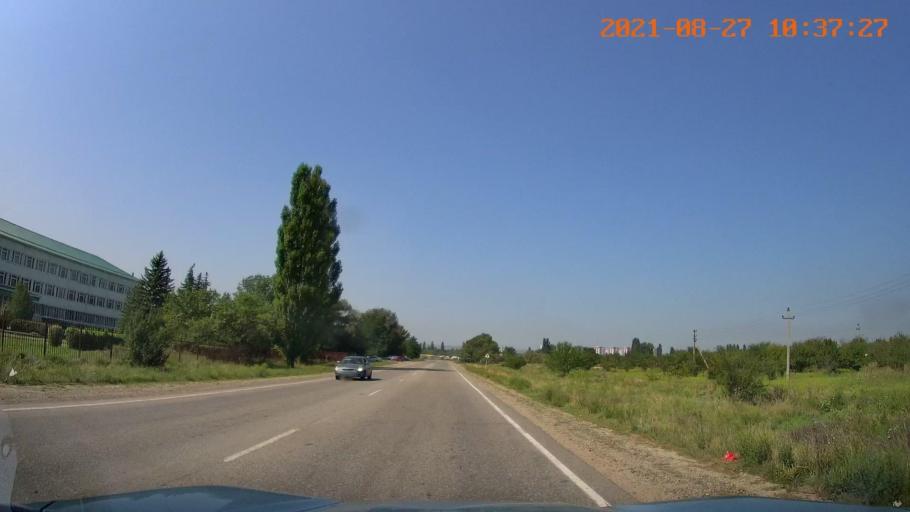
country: RU
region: Karachayevo-Cherkesiya
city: Cherkessk
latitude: 44.2543
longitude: 42.0776
